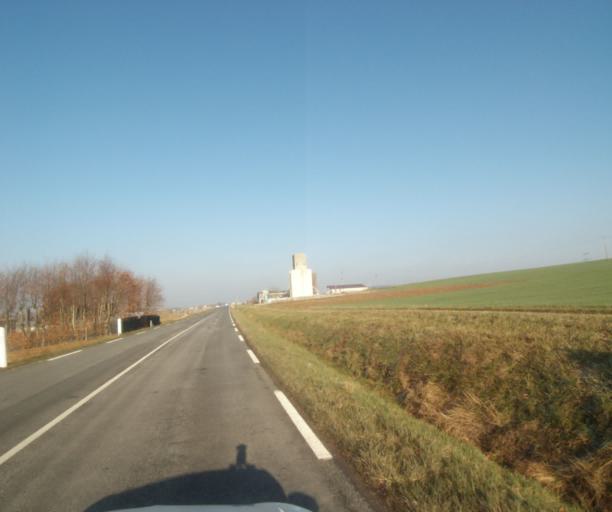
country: FR
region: Champagne-Ardenne
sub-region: Departement de la Haute-Marne
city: Wassy
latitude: 48.5110
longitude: 4.9379
